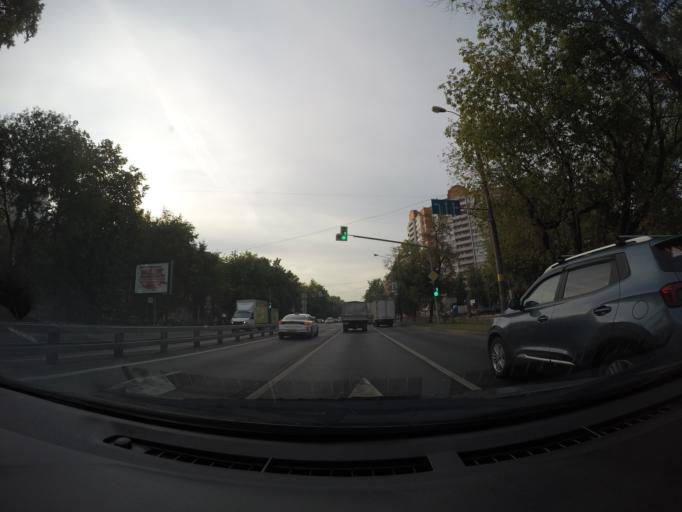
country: RU
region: Moscow
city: Zhulebino
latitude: 55.6942
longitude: 37.8637
